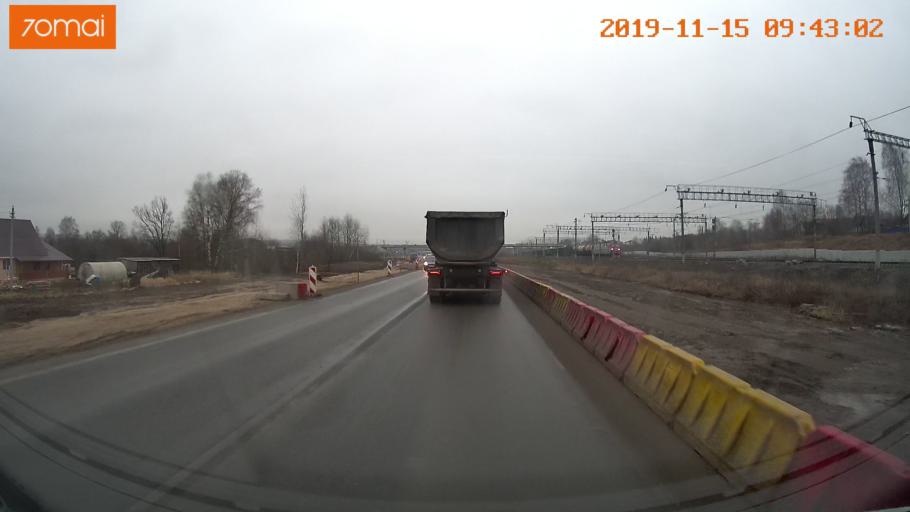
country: RU
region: Vologda
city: Sheksna
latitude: 59.2101
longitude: 38.5064
